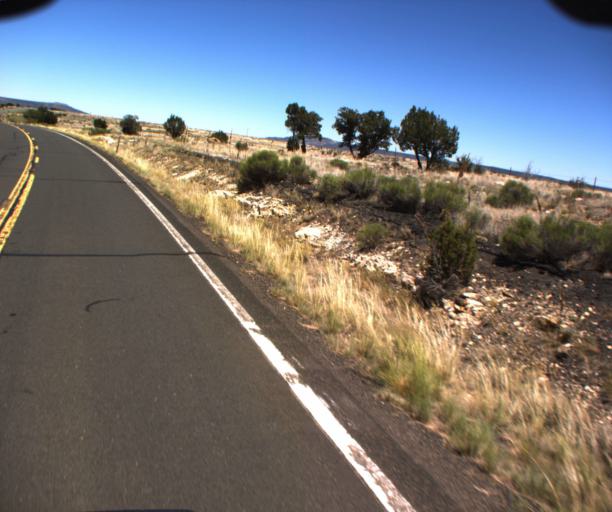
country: US
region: Arizona
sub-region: Coconino County
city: LeChee
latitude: 34.7693
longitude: -111.0081
